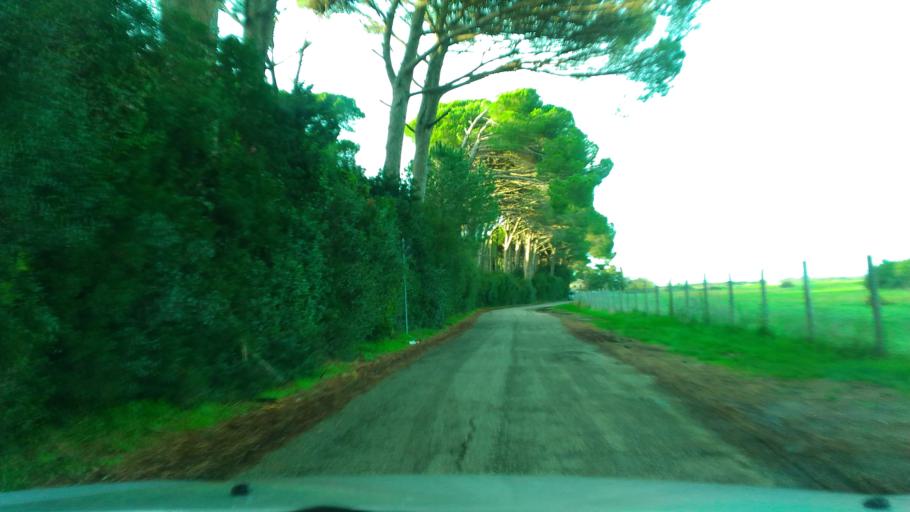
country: IT
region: Tuscany
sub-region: Provincia di Livorno
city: Cecina
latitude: 43.2787
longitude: 10.5148
